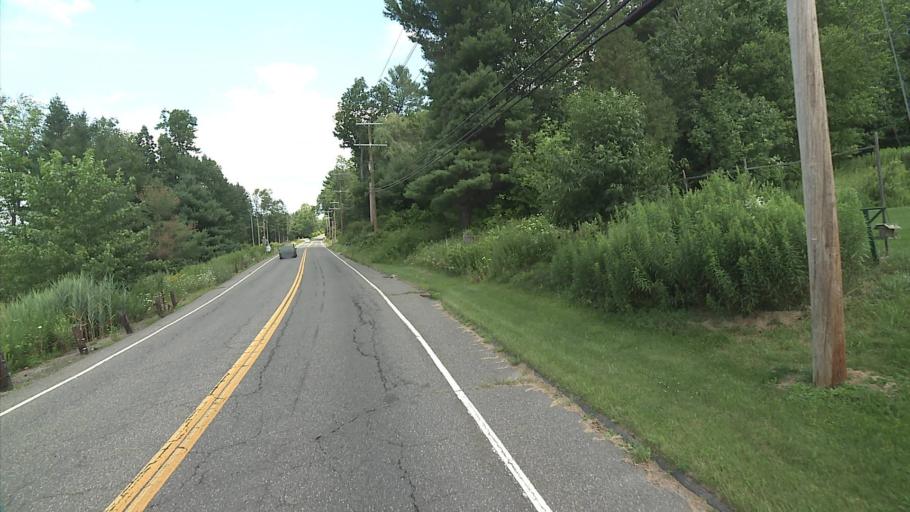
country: US
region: Connecticut
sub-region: Litchfield County
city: Winsted
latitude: 41.9492
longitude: -73.0438
